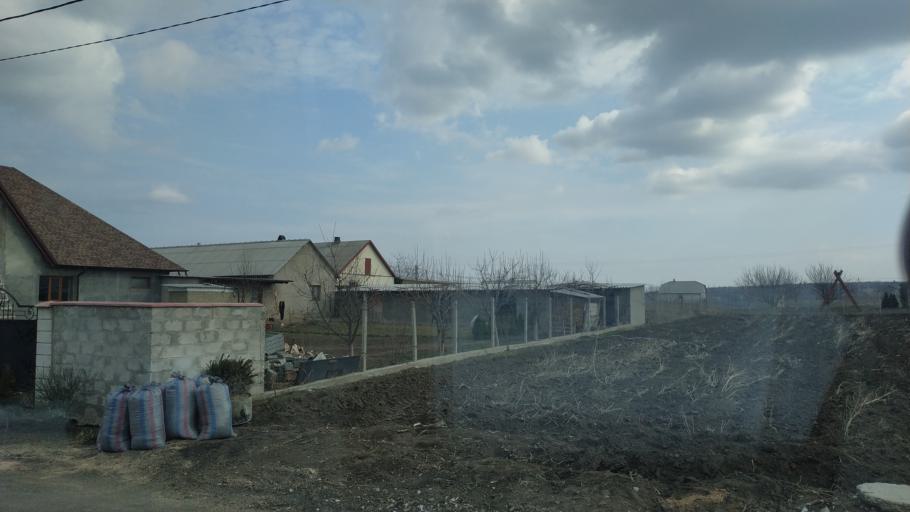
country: MD
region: Anenii Noi
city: Anenii Noi
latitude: 46.8969
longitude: 29.1325
